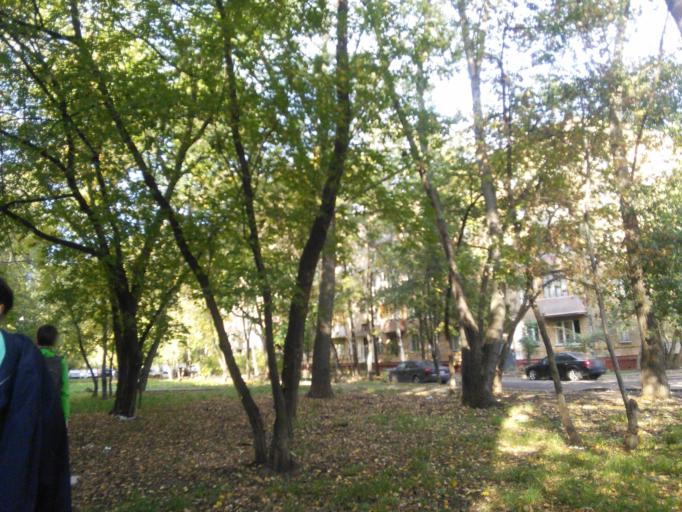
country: RU
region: Moscow
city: Mar'ina Roshcha
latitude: 55.8108
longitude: 37.5880
